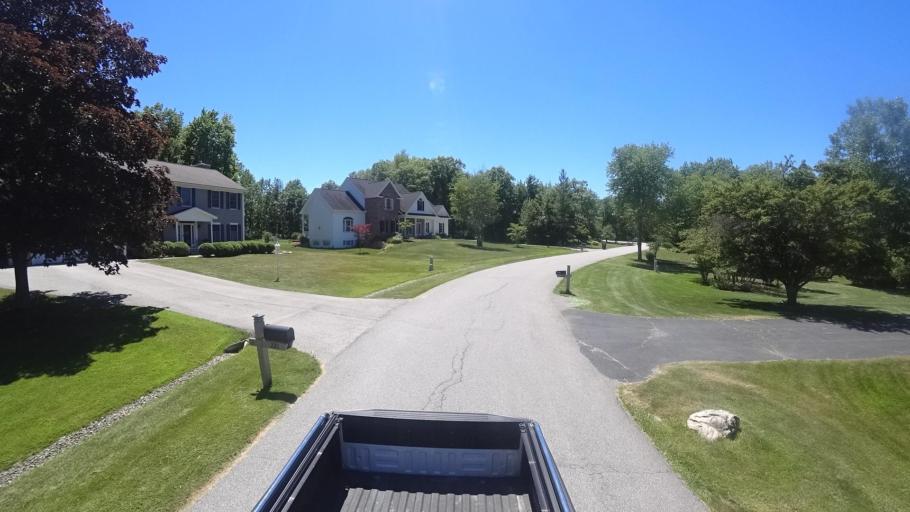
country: US
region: Indiana
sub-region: Porter County
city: Porter
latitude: 41.6339
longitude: -87.0798
